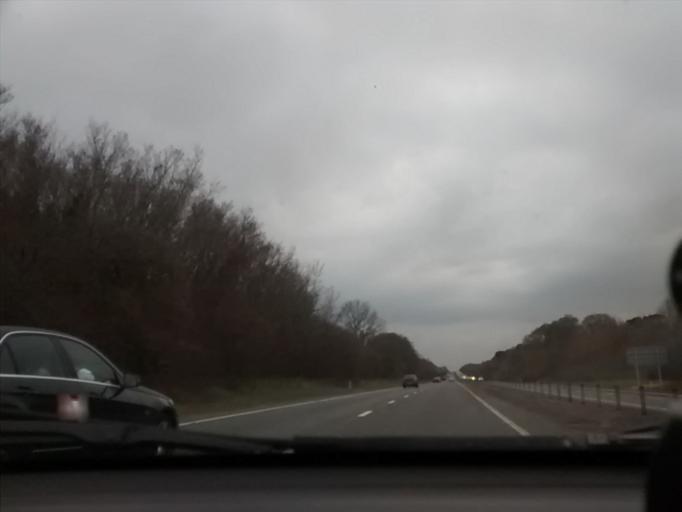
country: GB
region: England
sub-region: Cambridgeshire
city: Sawston
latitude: 52.1154
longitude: 0.2155
